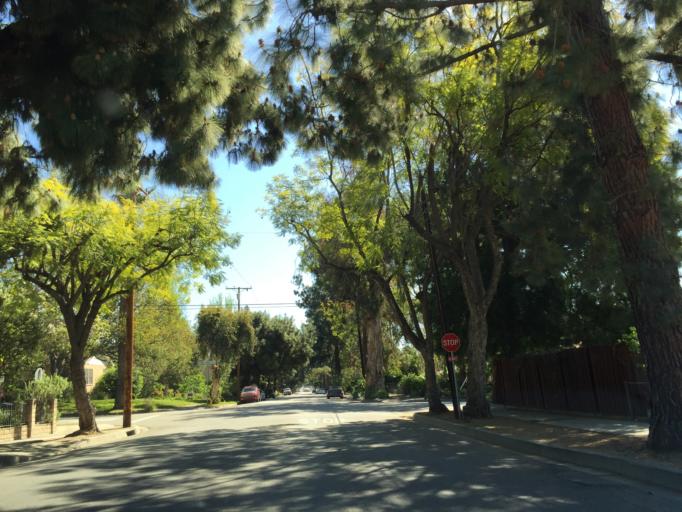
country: US
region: California
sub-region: Los Angeles County
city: Sierra Madre
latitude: 34.1642
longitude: -118.0652
